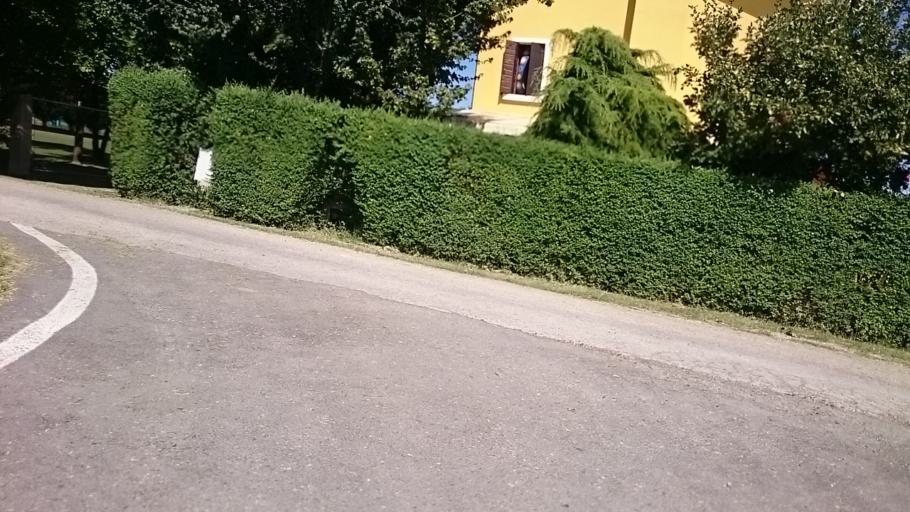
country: IT
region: Veneto
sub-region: Provincia di Venezia
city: Fiesso d'Artico
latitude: 45.4377
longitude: 12.0363
